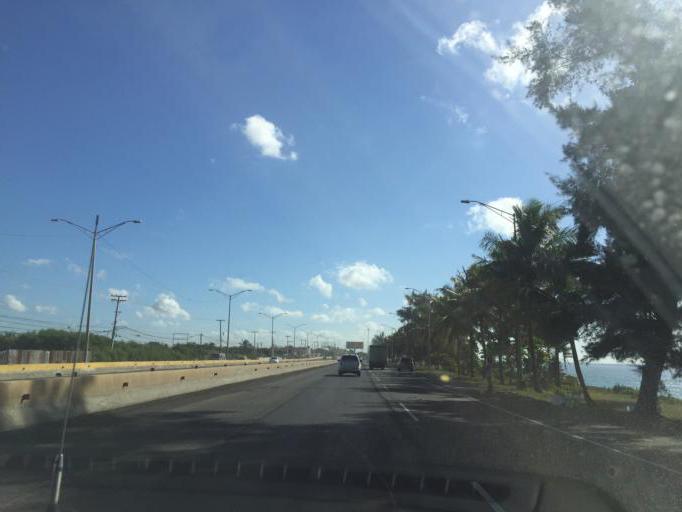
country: DO
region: Santo Domingo
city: Guerra
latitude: 18.4631
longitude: -69.7413
